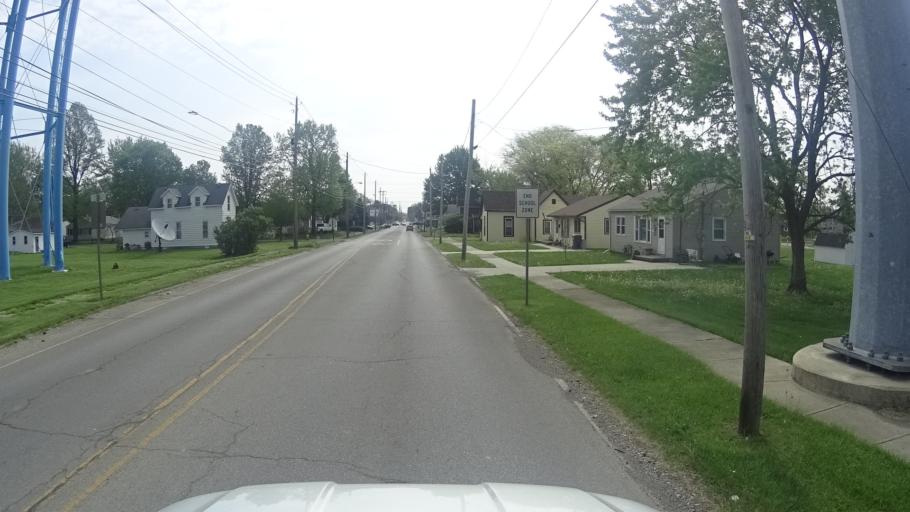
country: US
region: Indiana
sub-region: Madison County
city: Anderson
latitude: 40.1352
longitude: -85.6814
